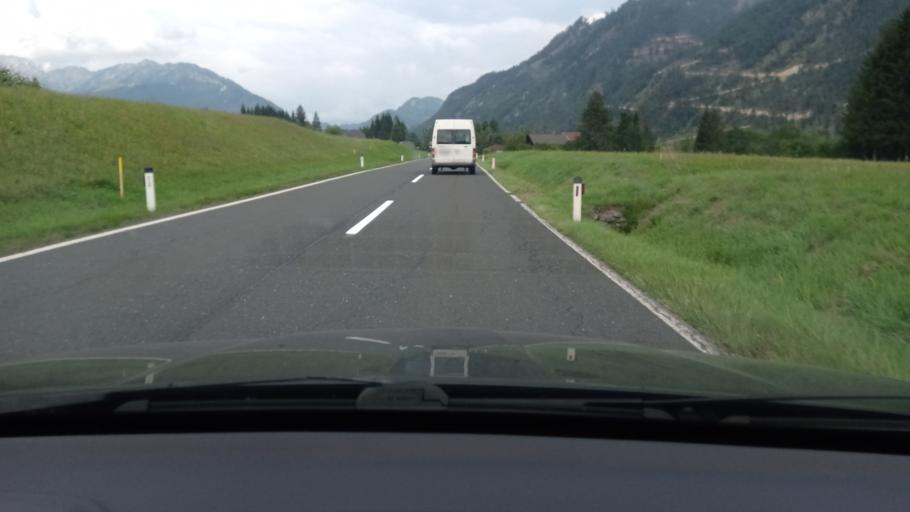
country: AT
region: Carinthia
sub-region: Politischer Bezirk Hermagor
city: Hermagor
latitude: 46.6639
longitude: 13.3072
